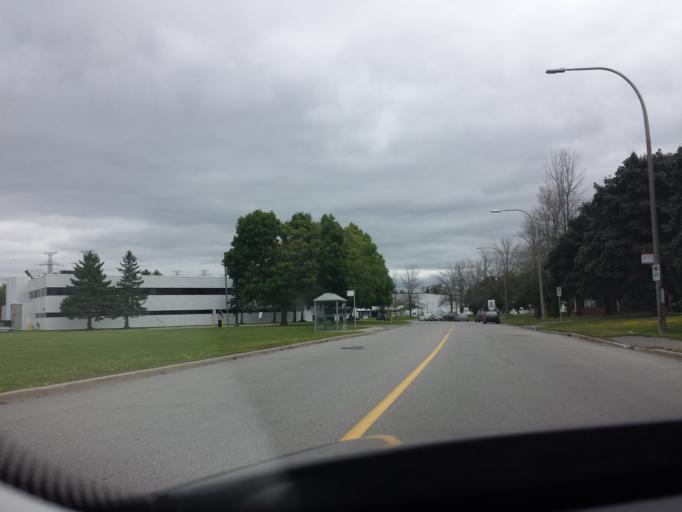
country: CA
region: Ontario
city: Ottawa
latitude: 45.3438
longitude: -75.7044
